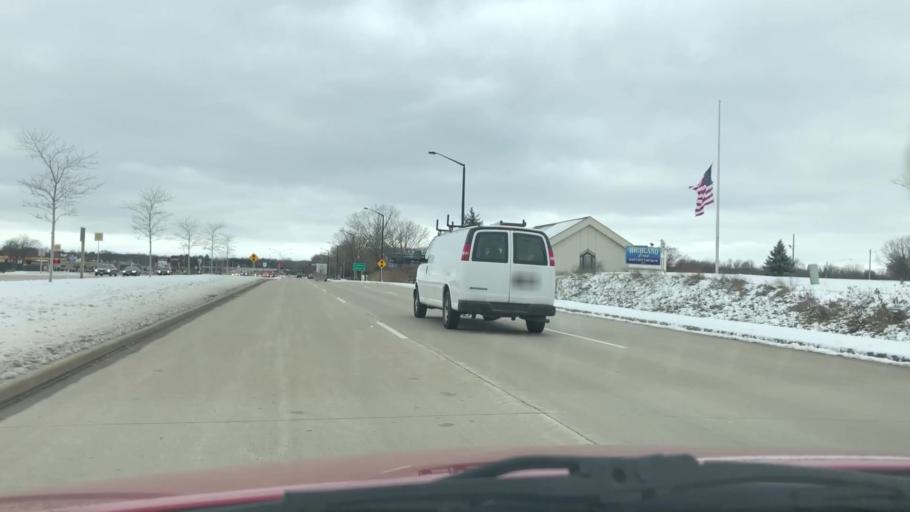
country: US
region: Wisconsin
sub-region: Brown County
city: Ashwaubenon
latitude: 44.5053
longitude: -88.0675
